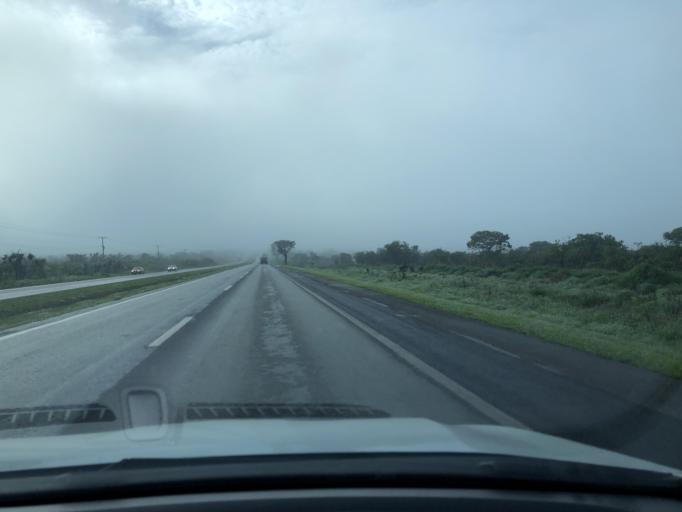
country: BR
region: Goias
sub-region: Luziania
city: Luziania
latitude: -16.2924
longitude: -47.8518
